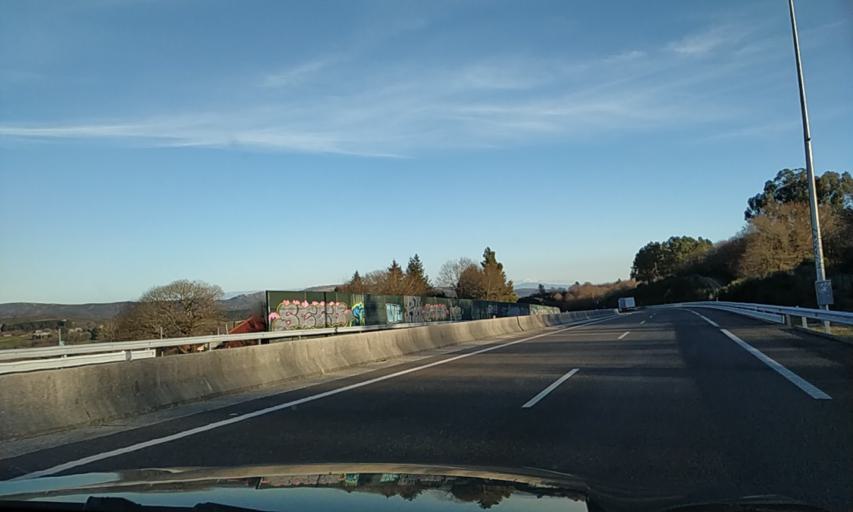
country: ES
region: Galicia
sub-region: Provincia de Pontevedra
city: Dozon
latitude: 42.5595
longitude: -8.0294
